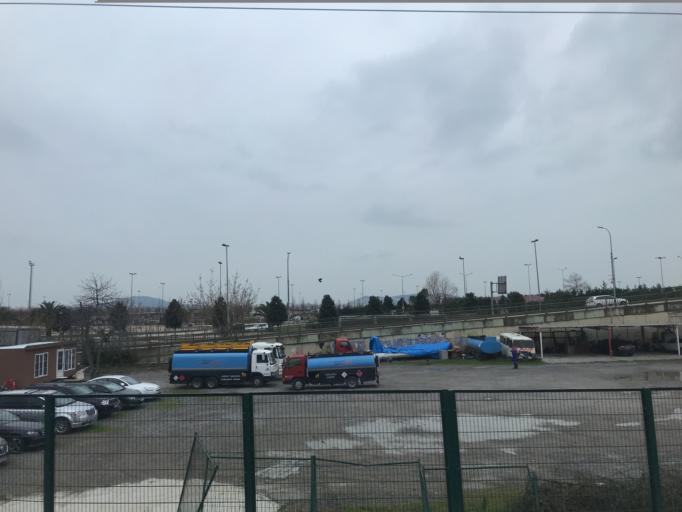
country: TR
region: Istanbul
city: Maltepe
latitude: 40.9329
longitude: 29.1182
